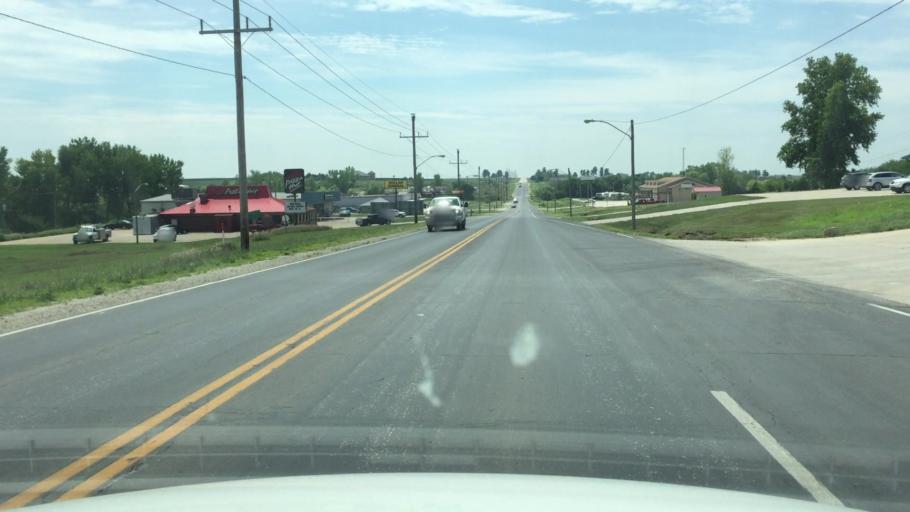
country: US
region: Kansas
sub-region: Nemaha County
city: Sabetha
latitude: 39.8933
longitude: -95.7883
